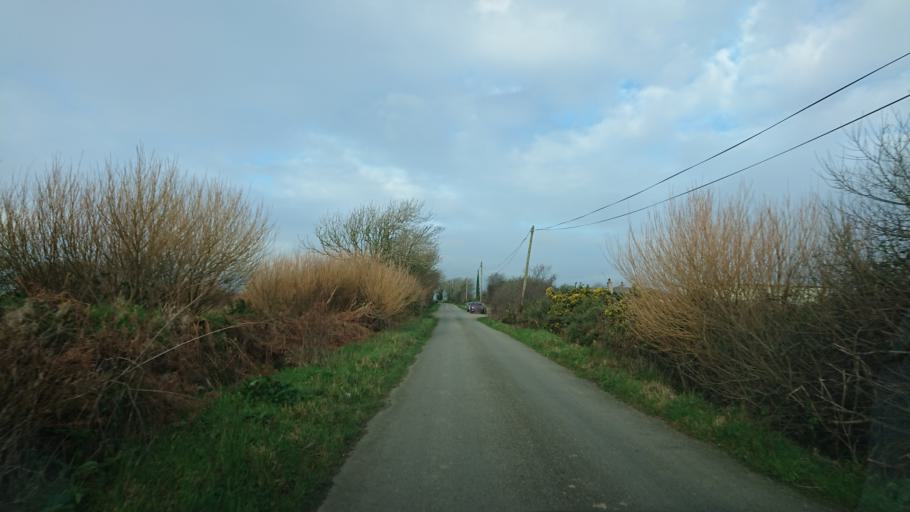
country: IE
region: Munster
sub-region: Waterford
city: Tra Mhor
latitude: 52.1455
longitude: -7.2079
